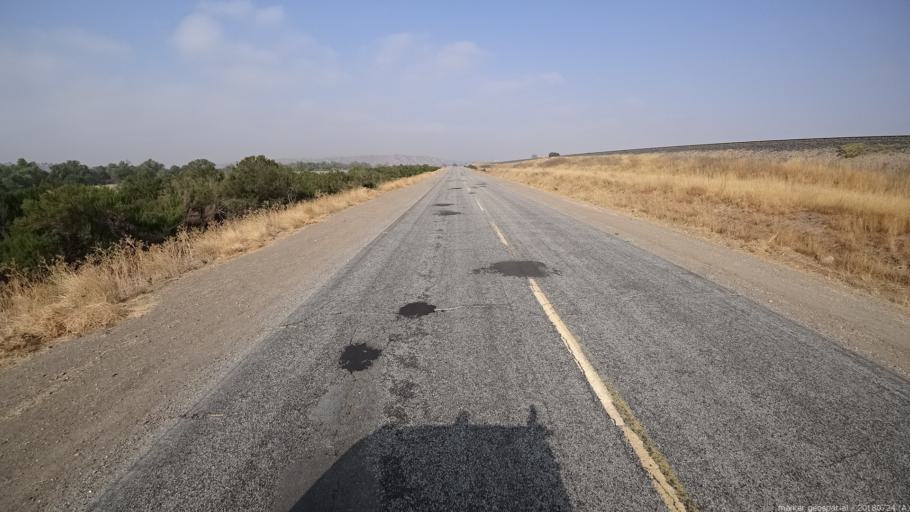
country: US
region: California
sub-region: San Luis Obispo County
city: San Miguel
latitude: 35.8621
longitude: -120.7745
